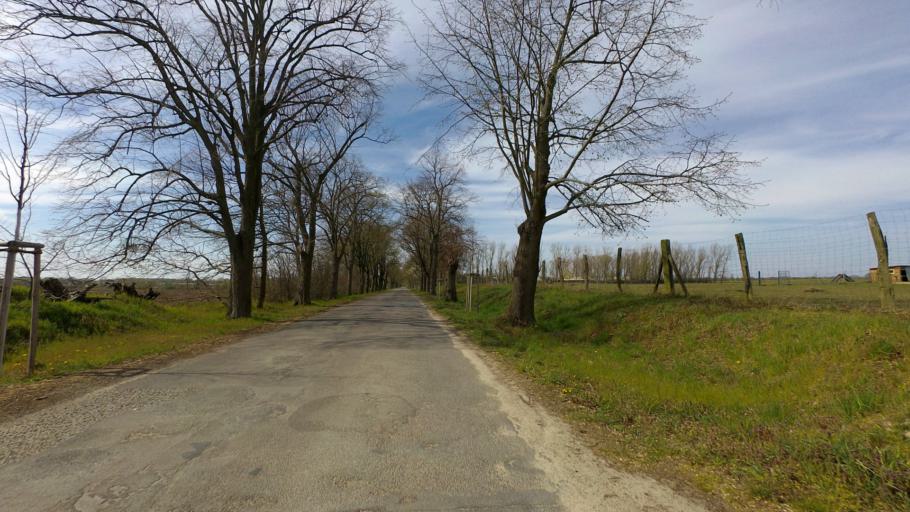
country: DE
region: Berlin
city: Marienfelde
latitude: 52.3831
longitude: 13.3454
